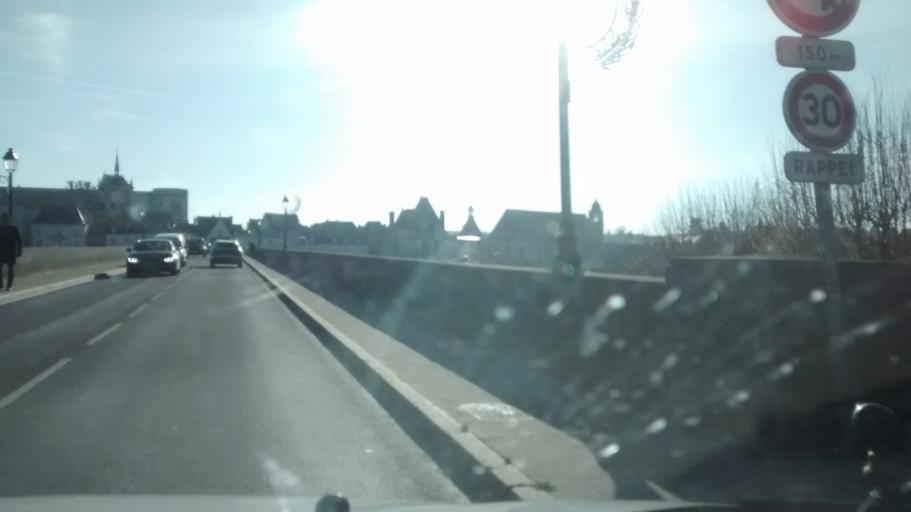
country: FR
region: Centre
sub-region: Departement d'Indre-et-Loire
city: Amboise
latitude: 47.4156
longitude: 0.9830
